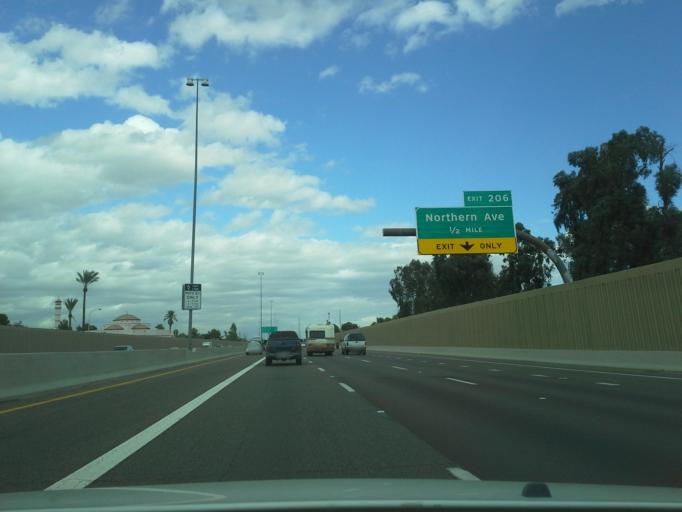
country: US
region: Arizona
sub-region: Maricopa County
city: Glendale
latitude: 33.5432
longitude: -112.1123
